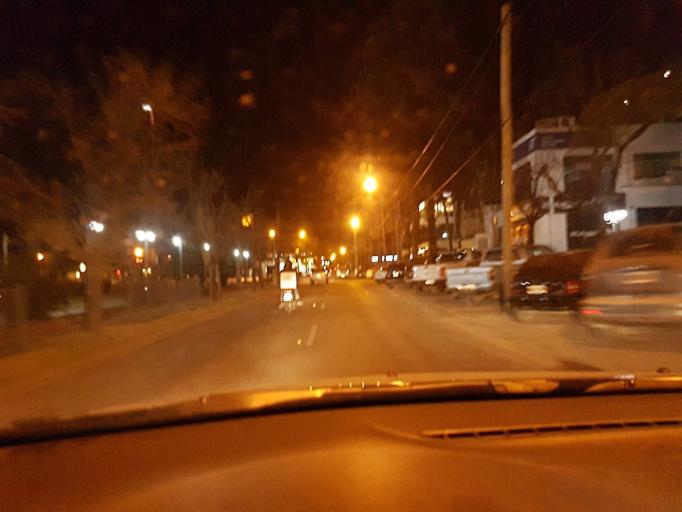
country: AR
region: Cordoba
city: Villa Allende
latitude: -31.2886
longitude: -64.2931
